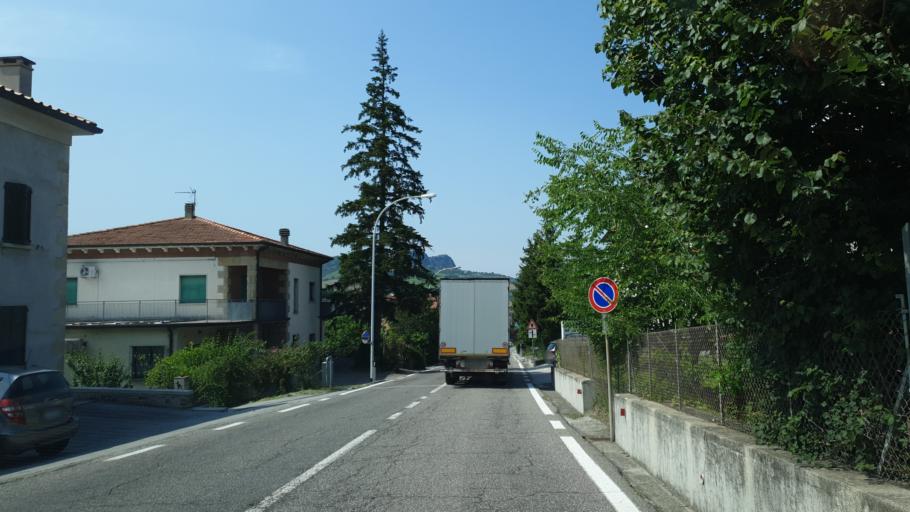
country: SM
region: Acquaviva
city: Acquaviva
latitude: 43.9504
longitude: 12.4068
